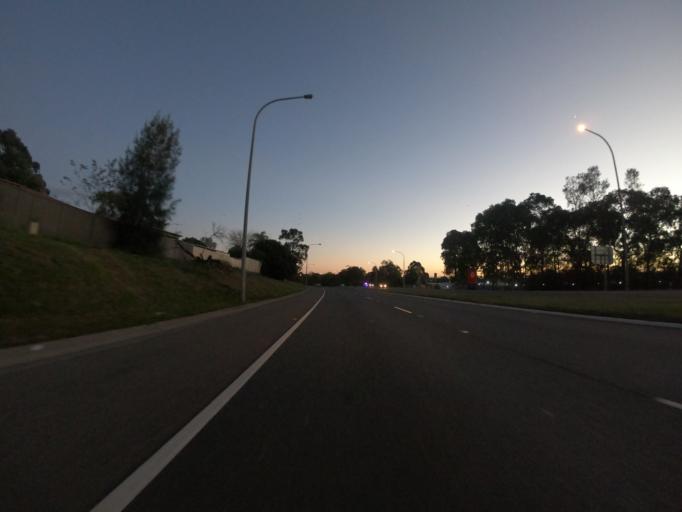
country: AU
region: New South Wales
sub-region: Campbelltown Municipality
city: Leumeah
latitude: -34.0434
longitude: 150.8294
